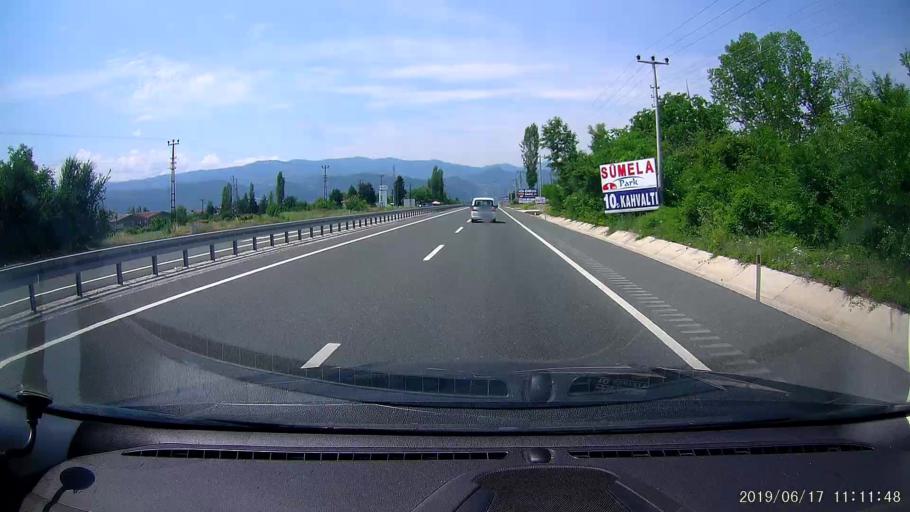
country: TR
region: Kastamonu
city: Tosya
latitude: 40.9817
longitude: 34.0047
